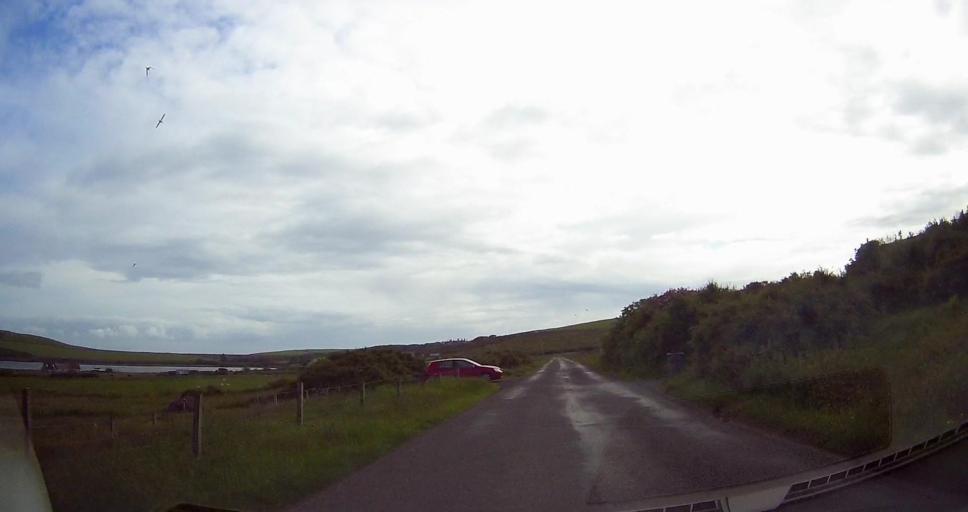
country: GB
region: Scotland
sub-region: Orkney Islands
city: Stromness
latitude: 58.7936
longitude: -3.2551
